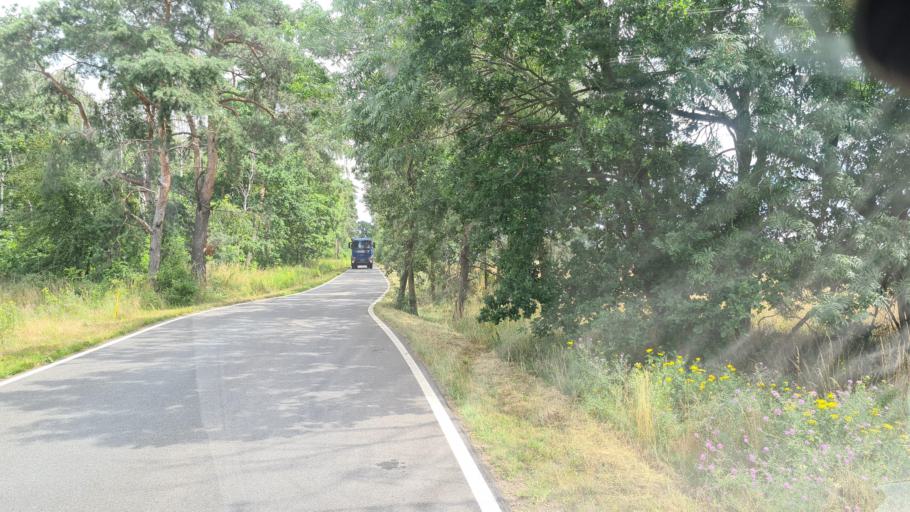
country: DE
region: Brandenburg
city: Grossraschen
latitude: 51.5677
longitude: 14.0732
